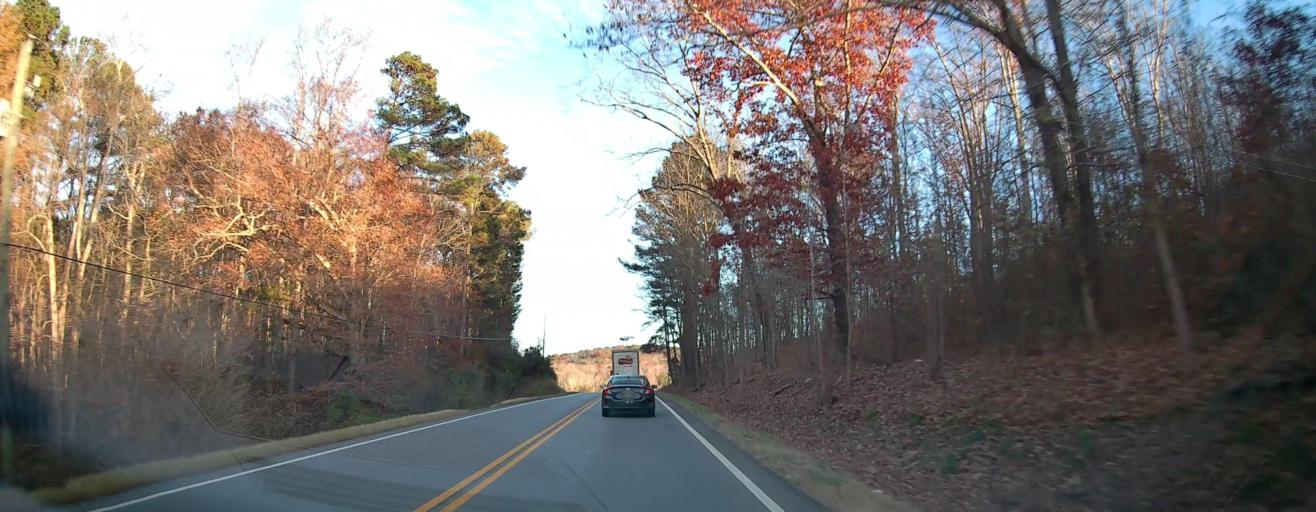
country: US
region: Alabama
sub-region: Saint Clair County
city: Steele
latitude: 34.0668
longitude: -86.2629
